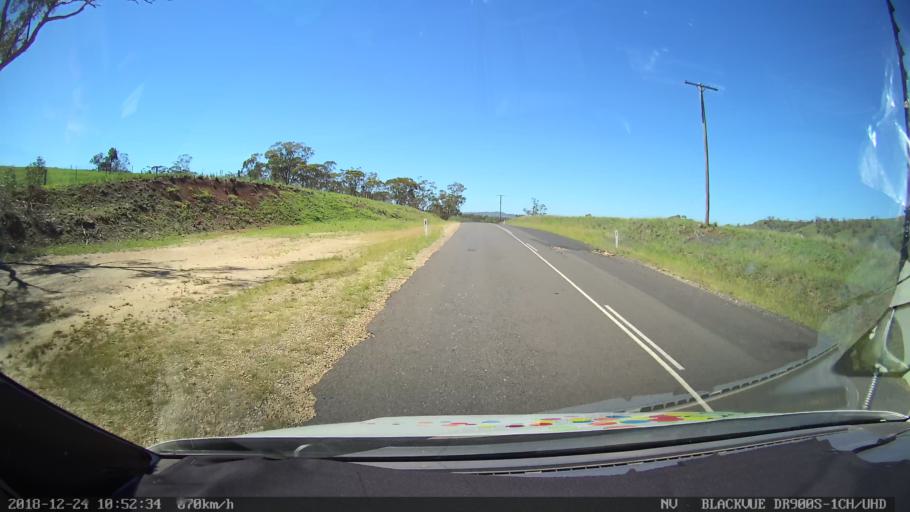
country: AU
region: New South Wales
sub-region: Upper Hunter Shire
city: Merriwa
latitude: -31.9819
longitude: 150.4223
